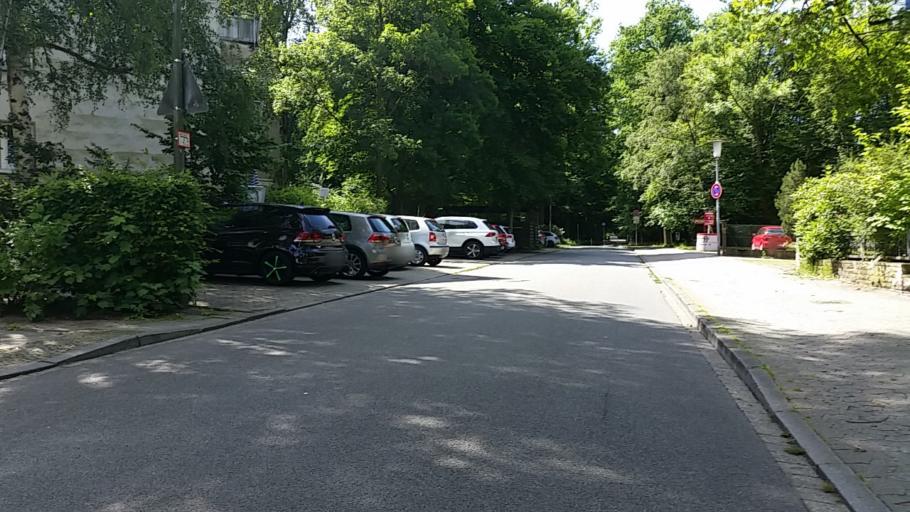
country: DE
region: Lower Saxony
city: Wolfsburg
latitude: 52.4196
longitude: 10.8069
